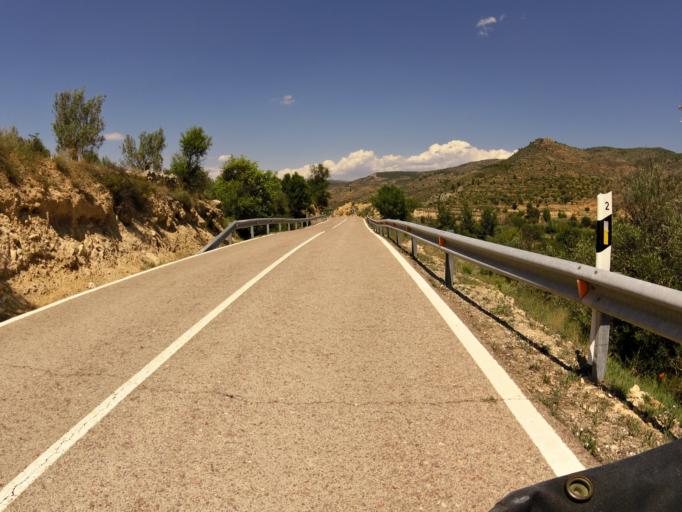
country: ES
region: Valencia
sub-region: Provincia de Valencia
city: Casas Bajas
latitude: 40.0165
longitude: -1.2658
